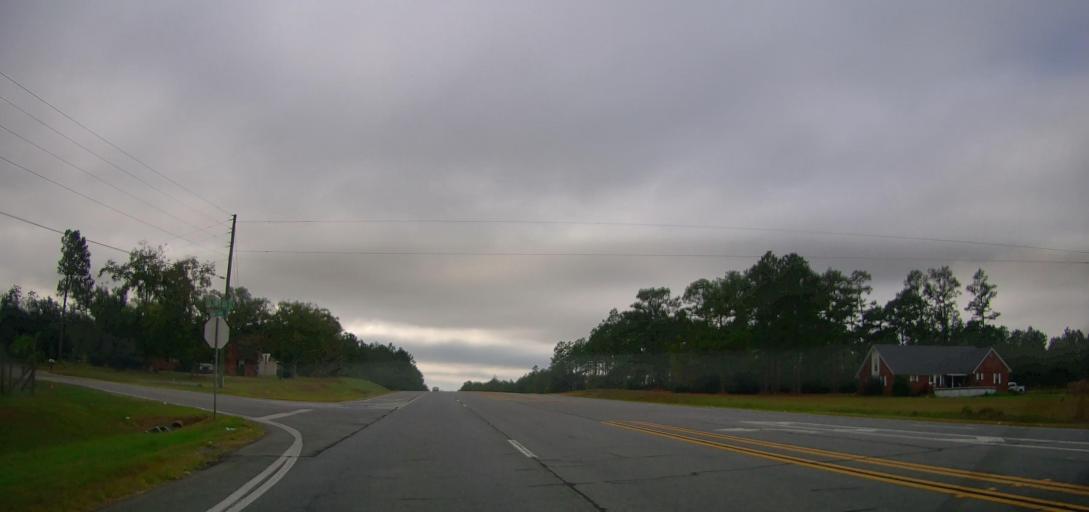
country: US
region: Georgia
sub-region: Colquitt County
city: Moultrie
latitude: 31.2526
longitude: -83.7142
